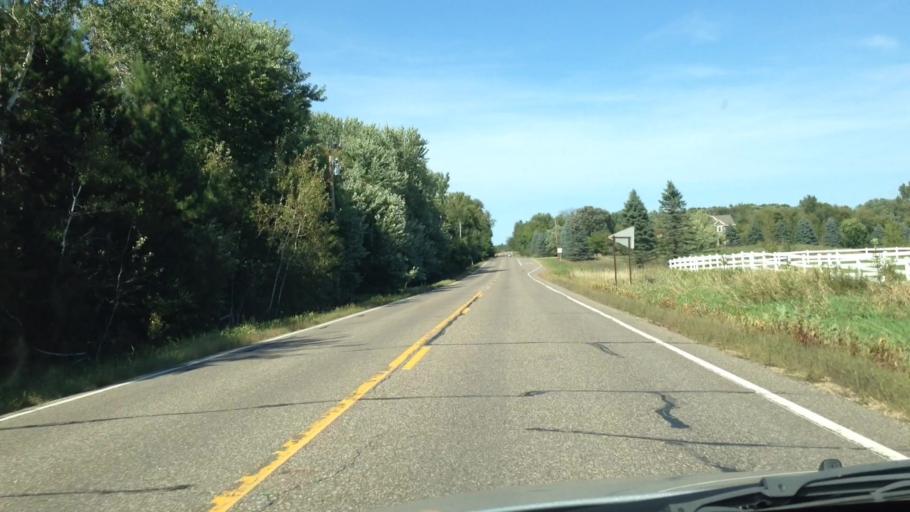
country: US
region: Minnesota
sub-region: Washington County
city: Stillwater
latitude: 45.1051
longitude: -92.8128
